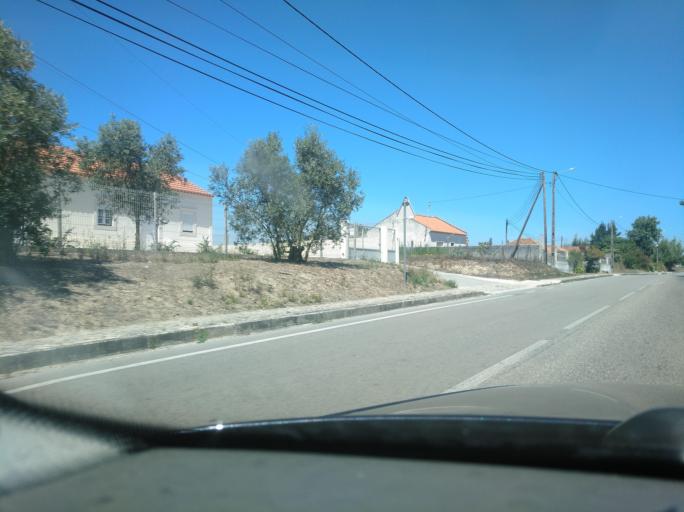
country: PT
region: Leiria
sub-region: Alcobaca
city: Aljubarrota
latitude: 39.5737
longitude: -8.9163
